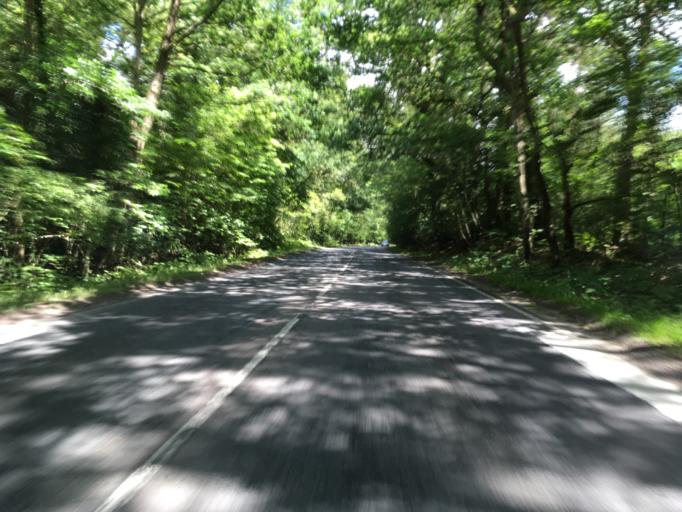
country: GB
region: England
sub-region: Hampshire
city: Highclere
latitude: 51.3568
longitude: -1.3667
